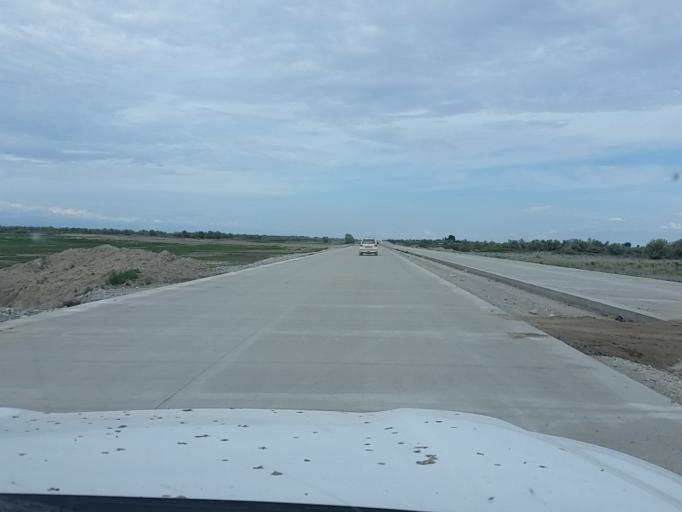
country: KZ
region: Almaty Oblysy
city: Zharkent
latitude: 44.0230
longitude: 79.8313
